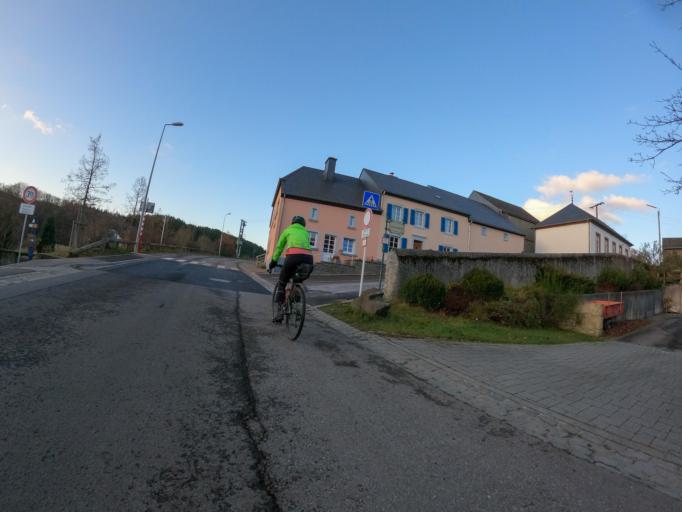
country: LU
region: Diekirch
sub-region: Canton de Wiltz
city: Bavigne
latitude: 49.9224
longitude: 5.8473
